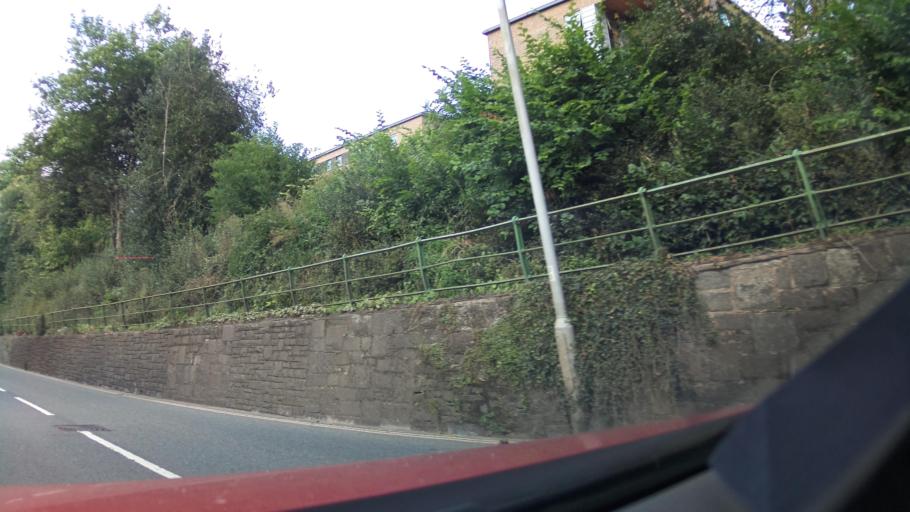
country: GB
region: England
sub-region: Devon
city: Exeter
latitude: 50.7397
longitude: -3.5455
